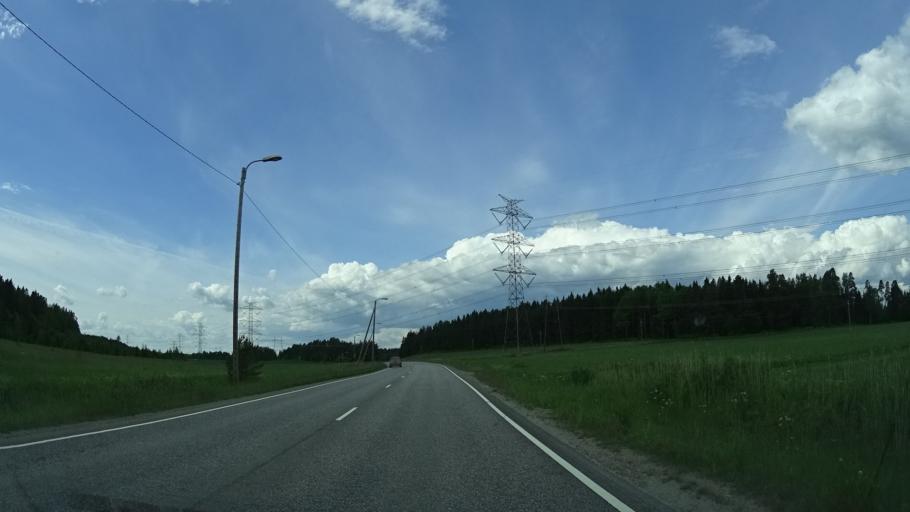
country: FI
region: Uusimaa
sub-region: Helsinki
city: Kirkkonummi
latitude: 60.2016
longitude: 24.5255
